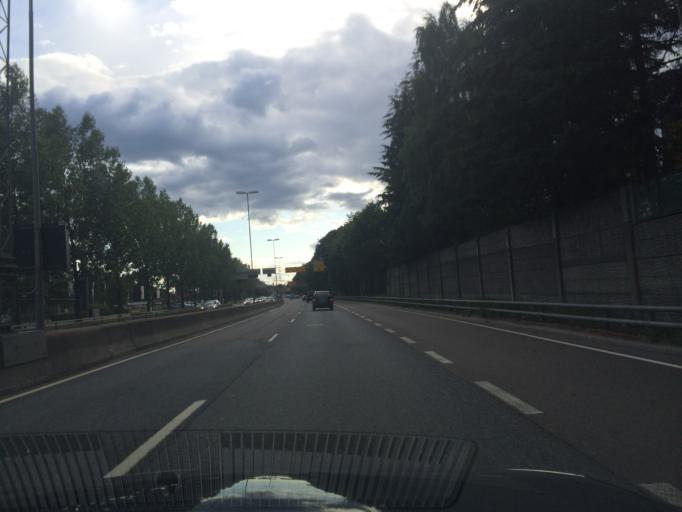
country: NO
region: Oslo
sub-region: Oslo
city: Oslo
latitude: 59.9506
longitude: 10.7348
